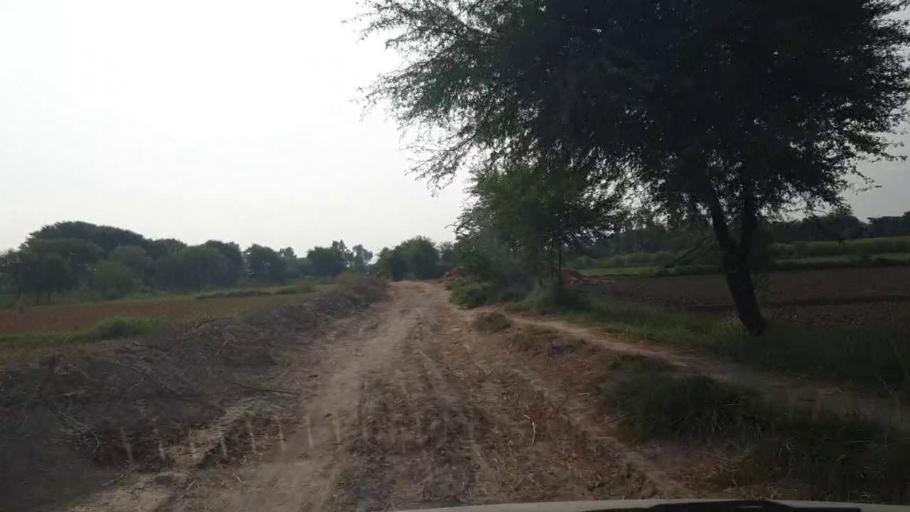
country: PK
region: Sindh
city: Rajo Khanani
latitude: 24.9064
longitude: 68.9208
